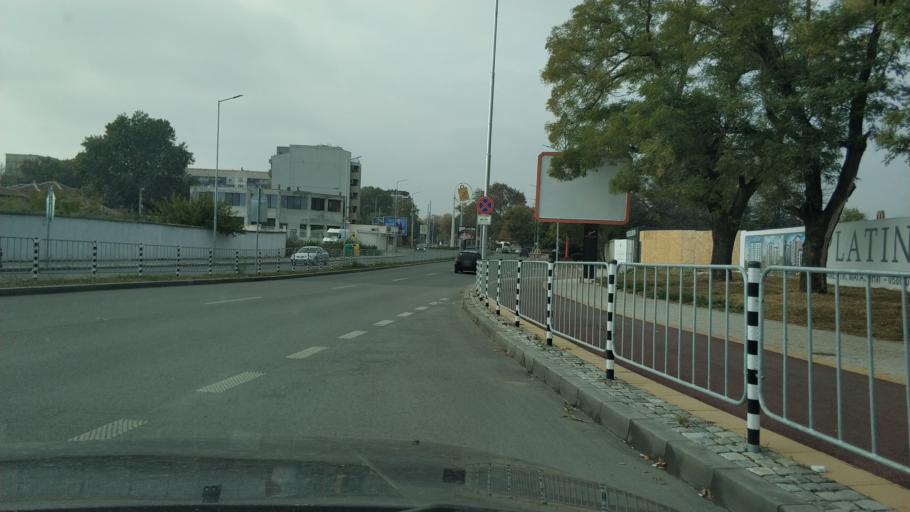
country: BG
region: Plovdiv
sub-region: Obshtina Plovdiv
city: Plovdiv
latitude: 42.1530
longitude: 24.7654
